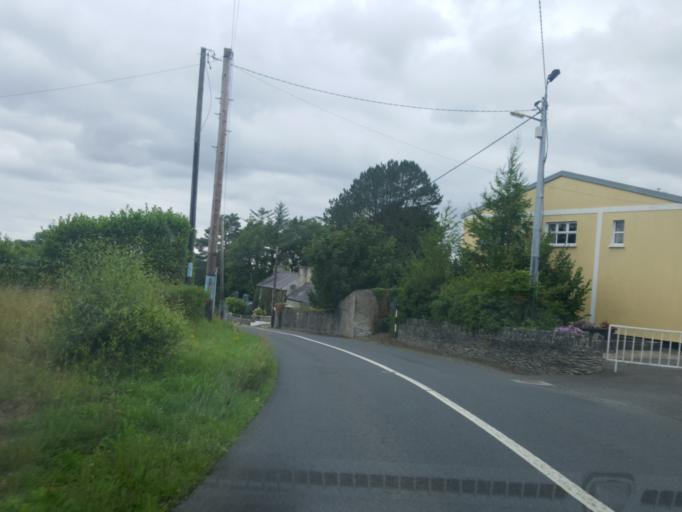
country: IE
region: Leinster
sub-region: Wicklow
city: Valleymount
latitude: 53.1317
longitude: -6.6076
